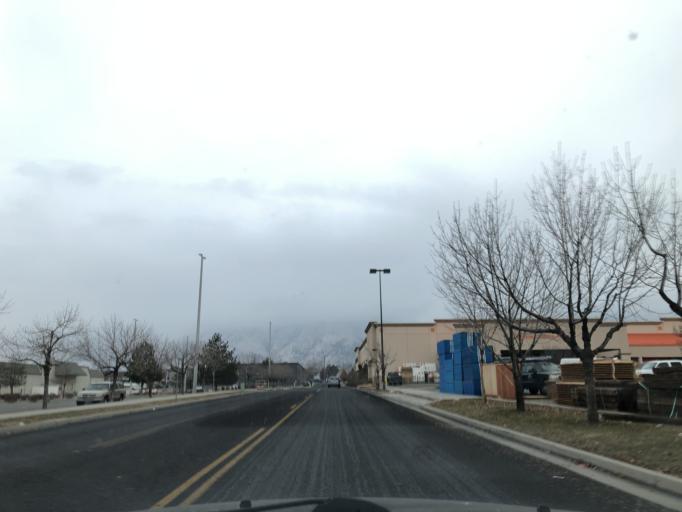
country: US
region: Utah
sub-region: Cache County
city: Logan
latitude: 41.7542
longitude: -111.8327
